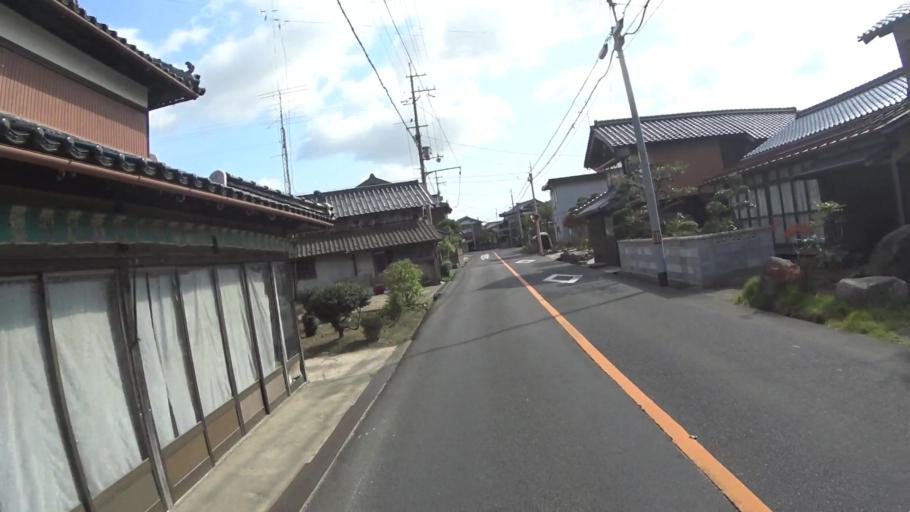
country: JP
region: Kyoto
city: Miyazu
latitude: 35.6129
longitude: 135.0837
